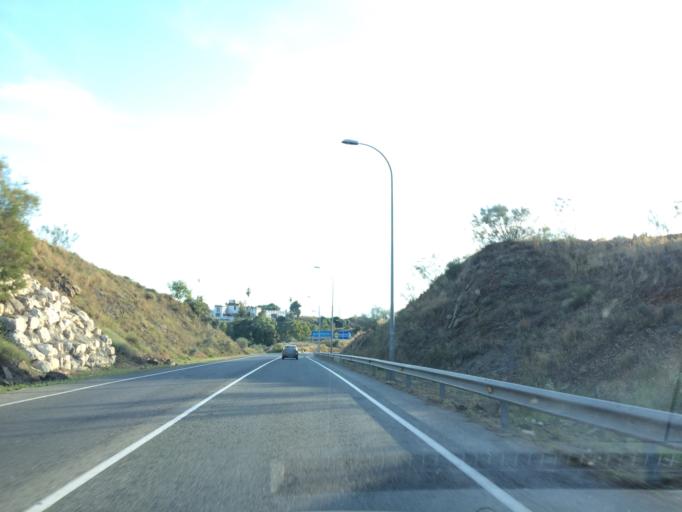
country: ES
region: Andalusia
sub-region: Provincia de Malaga
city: Malaga
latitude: 36.7413
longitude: -4.4079
